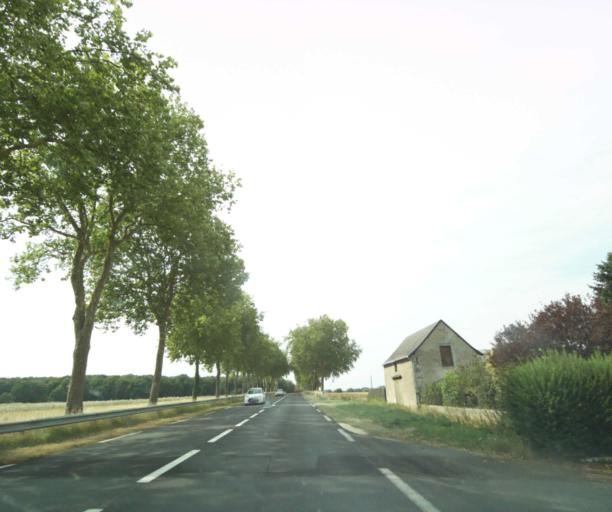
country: FR
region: Centre
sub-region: Departement d'Indre-et-Loire
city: Saint-Antoine-du-Rocher
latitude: 47.5031
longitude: 0.5993
